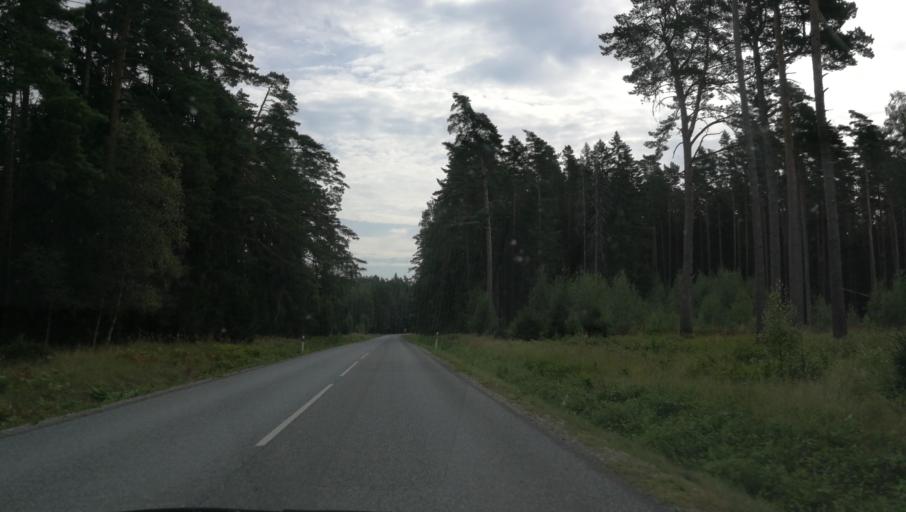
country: LV
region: Alsunga
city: Alsunga
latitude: 57.0132
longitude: 21.4294
